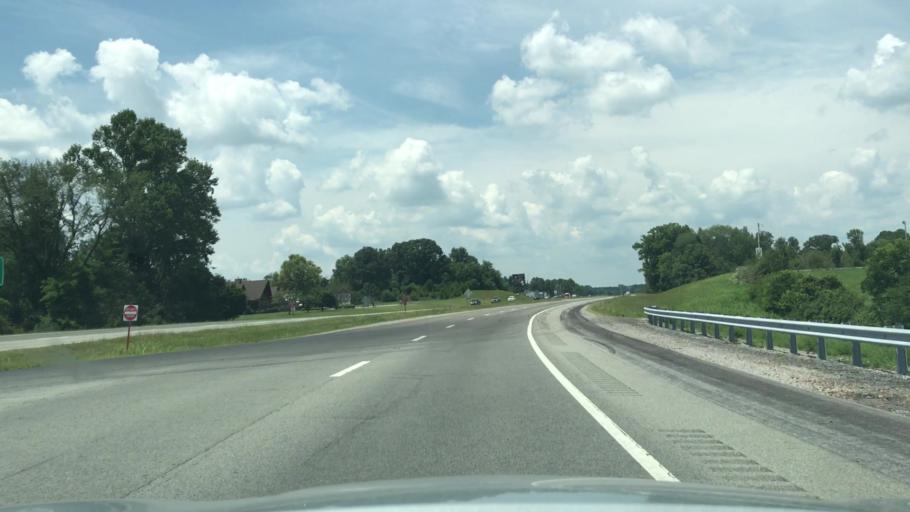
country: US
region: Tennessee
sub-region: Putnam County
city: Algood
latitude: 36.2073
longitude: -85.4355
